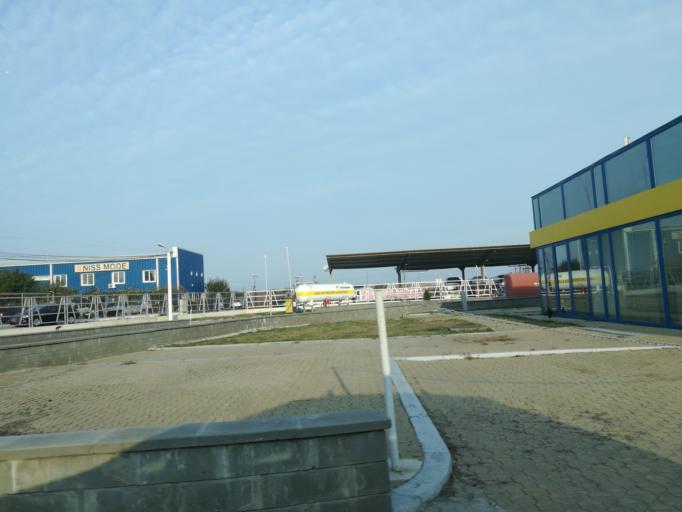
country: RO
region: Constanta
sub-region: Municipiul Constanta
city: Palazu Mare
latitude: 44.2043
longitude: 28.6112
